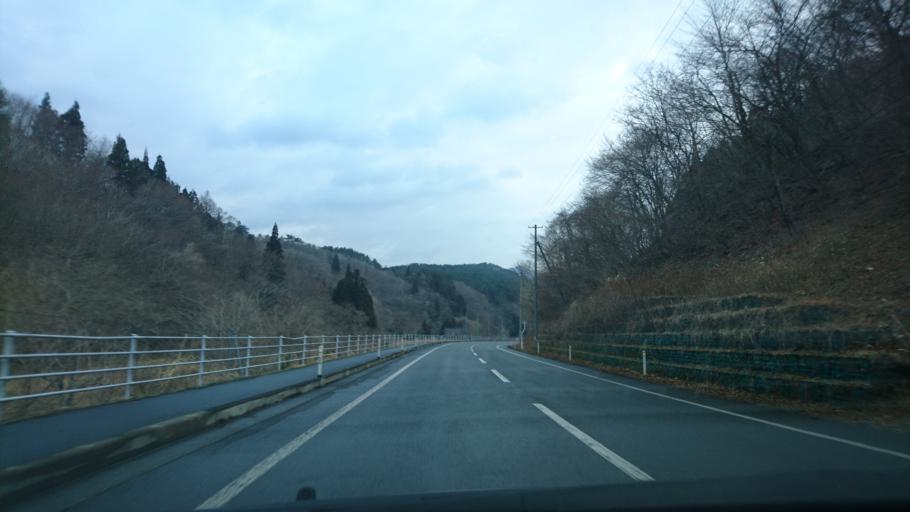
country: JP
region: Iwate
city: Ofunato
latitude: 39.0050
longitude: 141.5444
